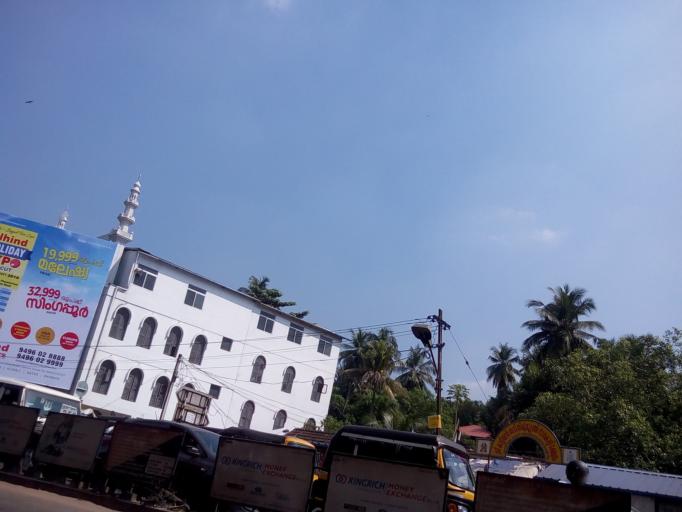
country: IN
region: Kerala
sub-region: Kozhikode
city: Kozhikode
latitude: 11.2557
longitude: 75.7865
